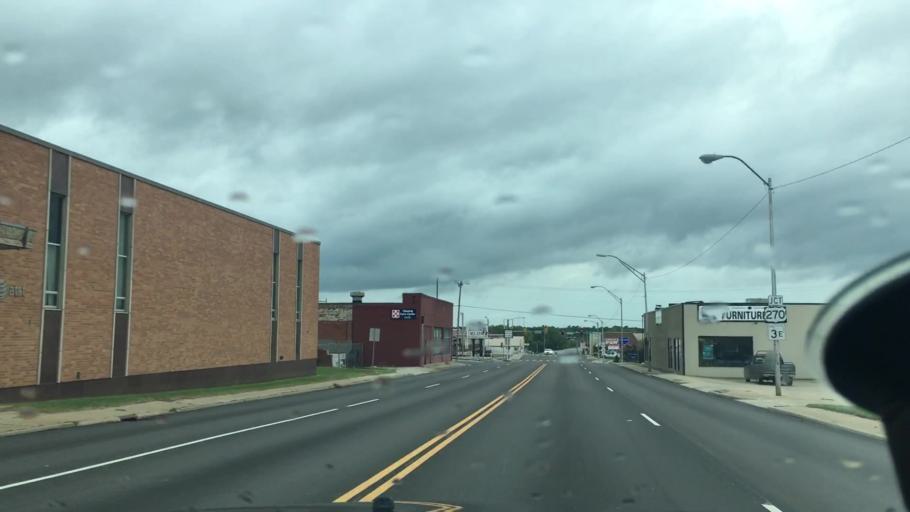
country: US
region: Oklahoma
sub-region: Seminole County
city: Seminole
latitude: 35.2265
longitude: -96.6711
